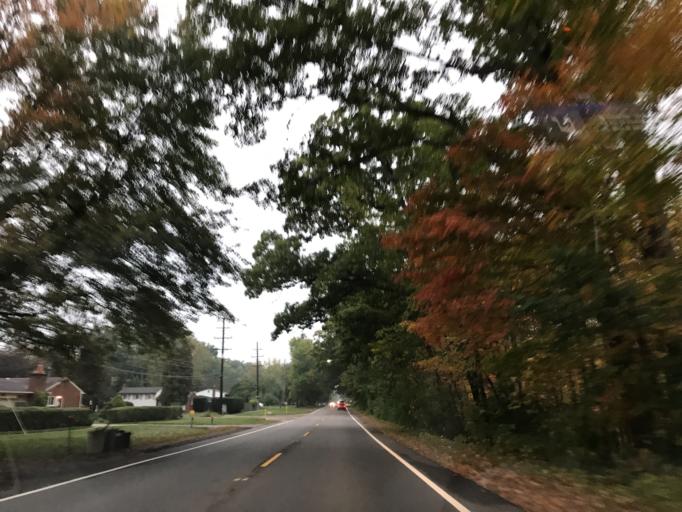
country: US
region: Michigan
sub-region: Oakland County
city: Farmington
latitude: 42.4565
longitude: -83.3202
